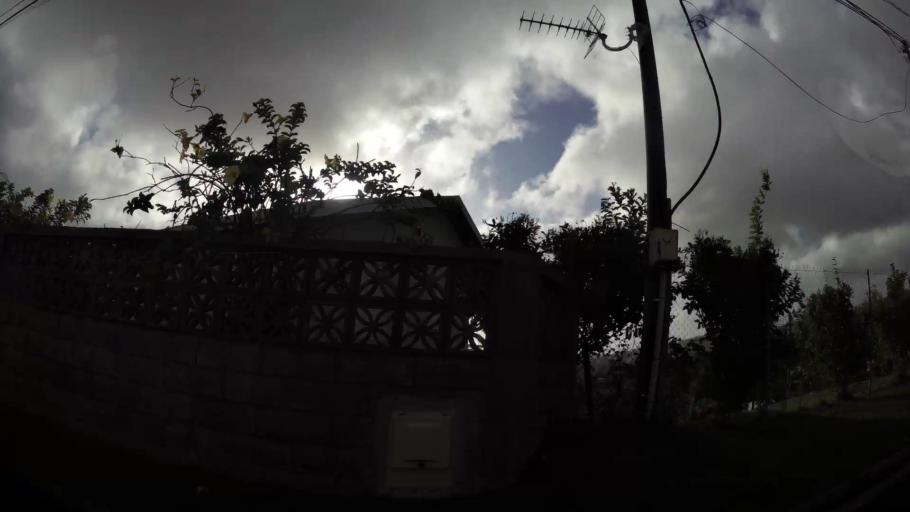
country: MQ
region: Martinique
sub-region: Martinique
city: Fort-de-France
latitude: 14.6263
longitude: -61.0813
